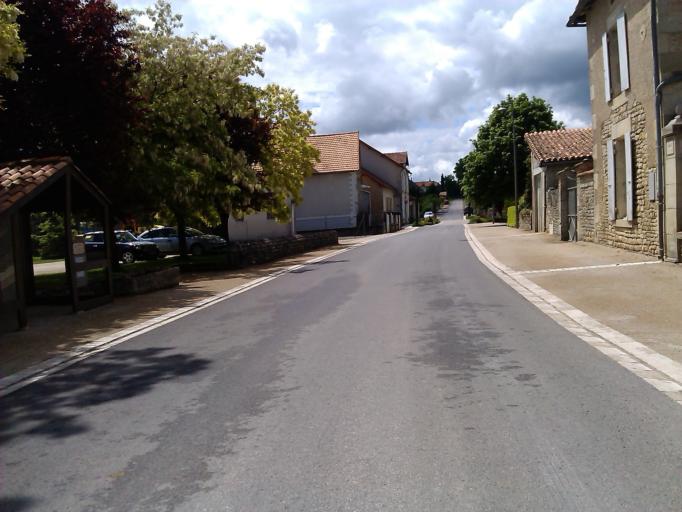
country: FR
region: Poitou-Charentes
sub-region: Departement de la Charente
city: Champagne-Mouton
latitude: 46.0373
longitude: 0.4517
